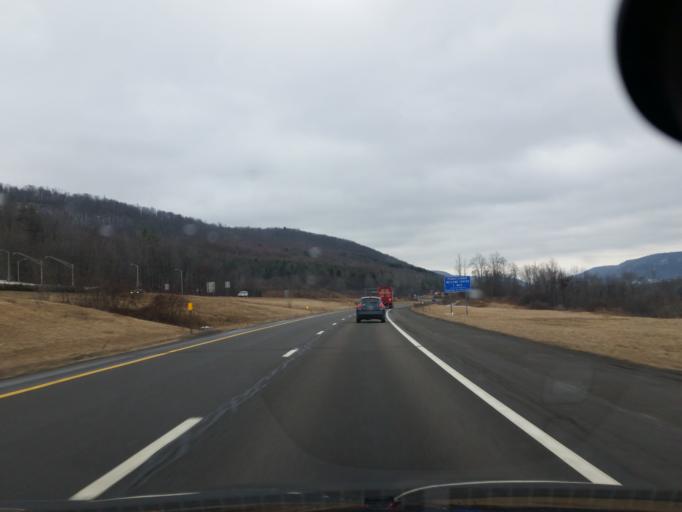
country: US
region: Pennsylvania
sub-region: Susquehanna County
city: Hallstead
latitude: 42.0029
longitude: -75.7542
